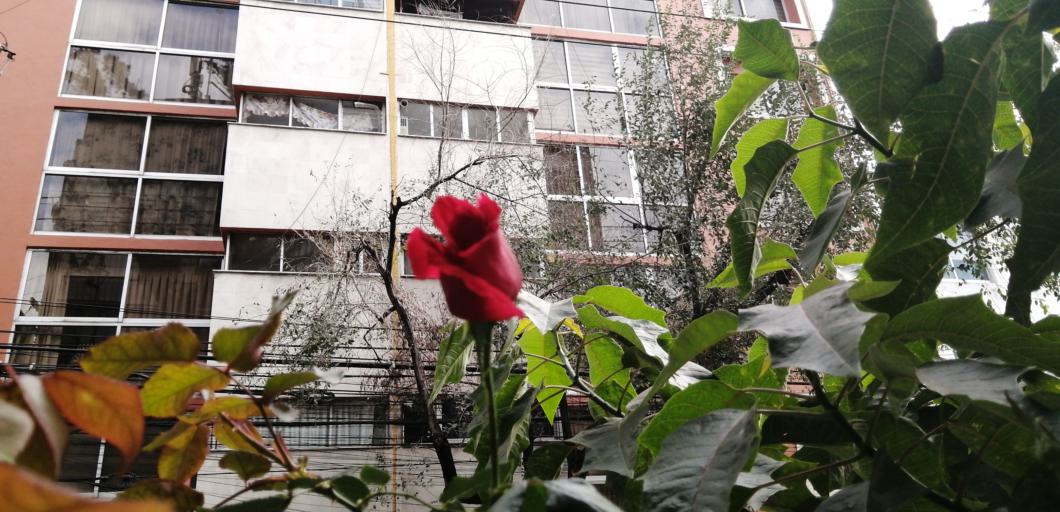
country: MX
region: Mexico City
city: Colonia del Valle
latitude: 19.3961
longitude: -99.1763
